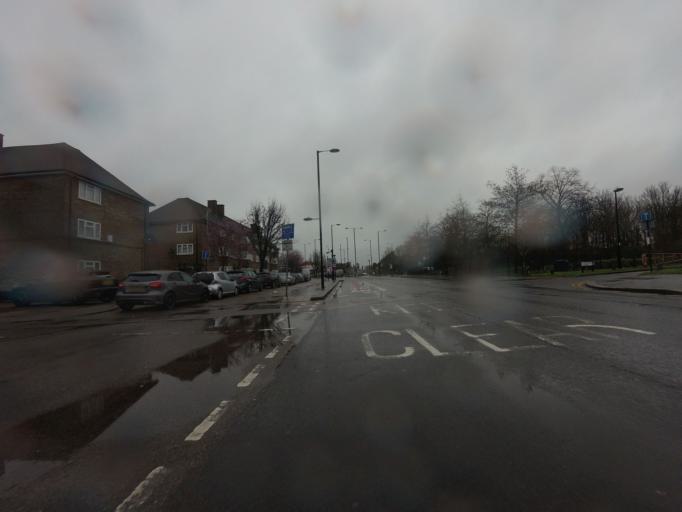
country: GB
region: England
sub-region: Hertfordshire
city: Waltham Cross
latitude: 51.6791
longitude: -0.0342
